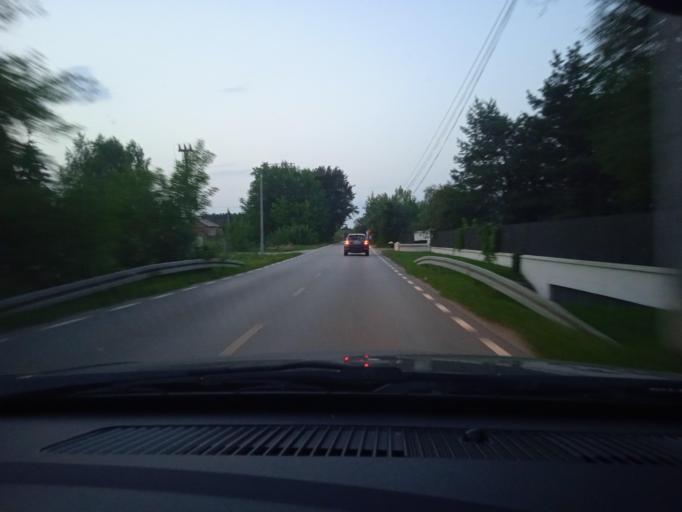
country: PL
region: Masovian Voivodeship
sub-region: Powiat nowodworski
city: Pomiechowek
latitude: 52.5170
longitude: 20.6797
